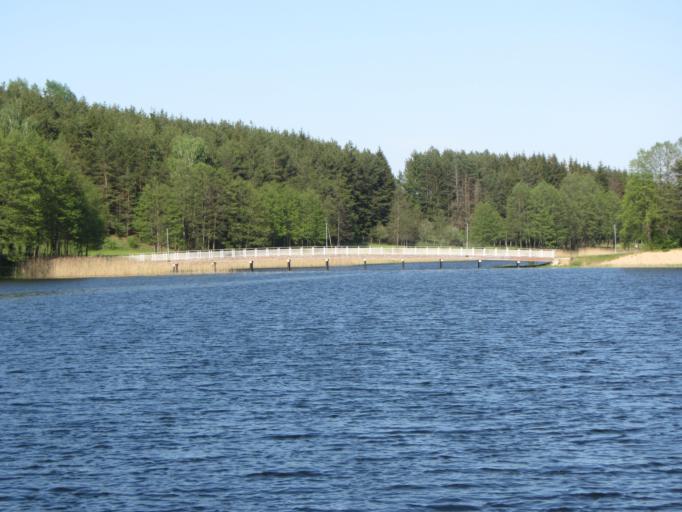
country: LT
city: Moletai
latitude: 55.2322
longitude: 25.4285
